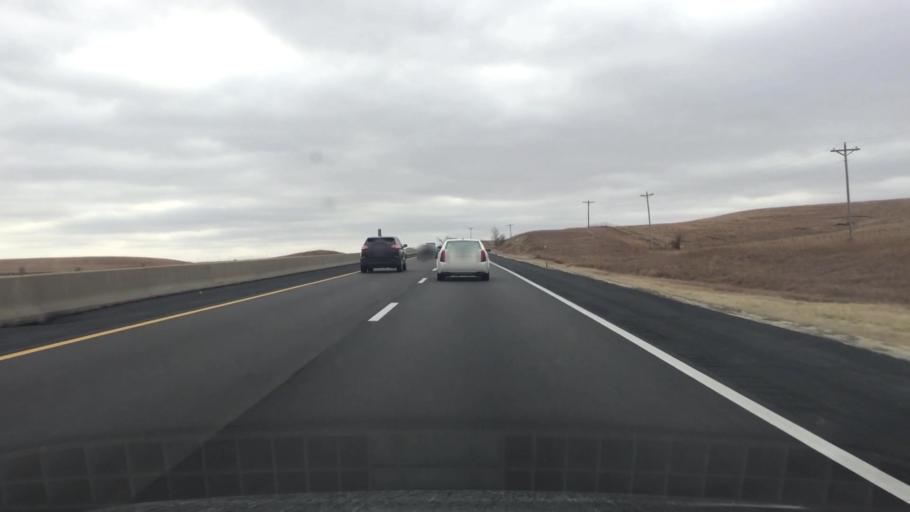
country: US
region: Kansas
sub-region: Chase County
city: Cottonwood Falls
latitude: 38.1167
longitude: -96.5678
